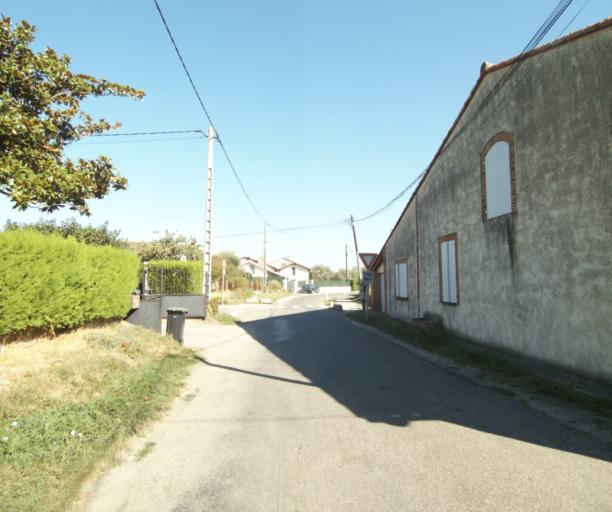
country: FR
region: Midi-Pyrenees
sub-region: Departement du Tarn-et-Garonne
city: Verdun-sur-Garonne
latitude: 43.8496
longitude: 1.2290
